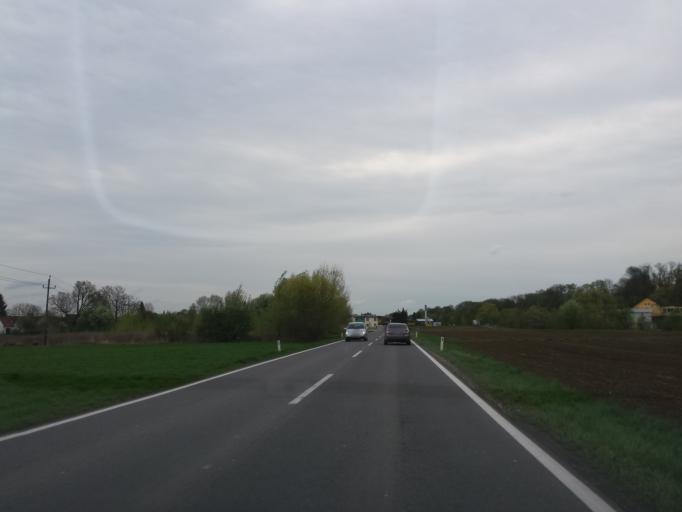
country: AT
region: Styria
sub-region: Politischer Bezirk Hartberg-Fuerstenfeld
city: Fuerstenfeld
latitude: 47.0507
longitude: 16.0848
